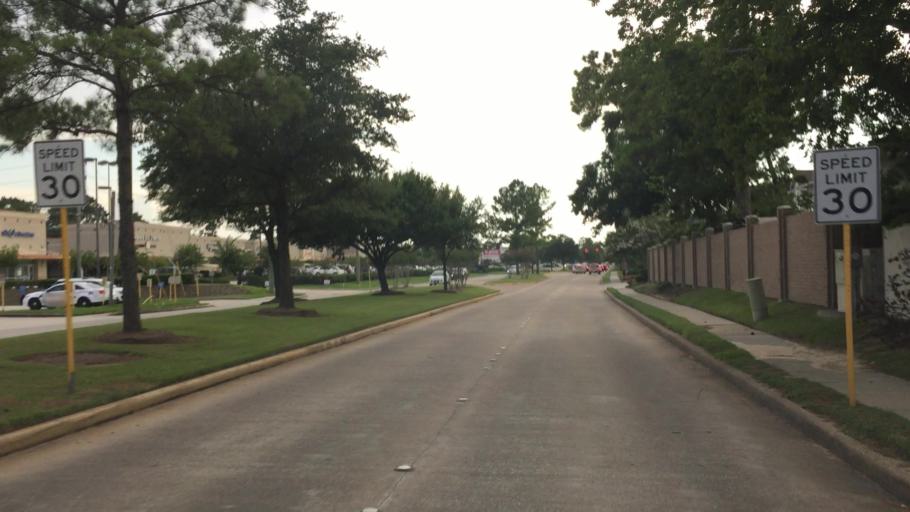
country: US
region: Texas
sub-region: Harris County
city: Hudson
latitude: 30.0124
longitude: -95.5118
